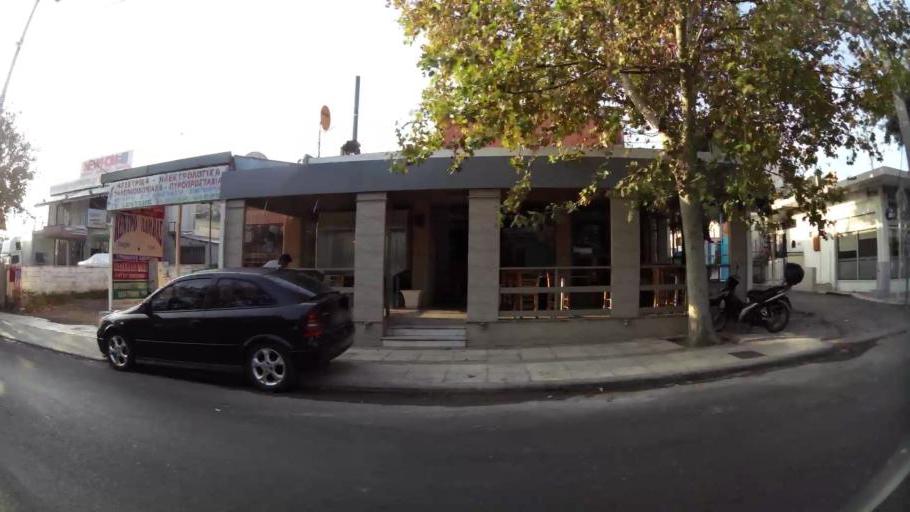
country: GR
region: Attica
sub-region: Nomarchia Dytikis Attikis
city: Zefyri
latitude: 38.0691
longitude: 23.7089
